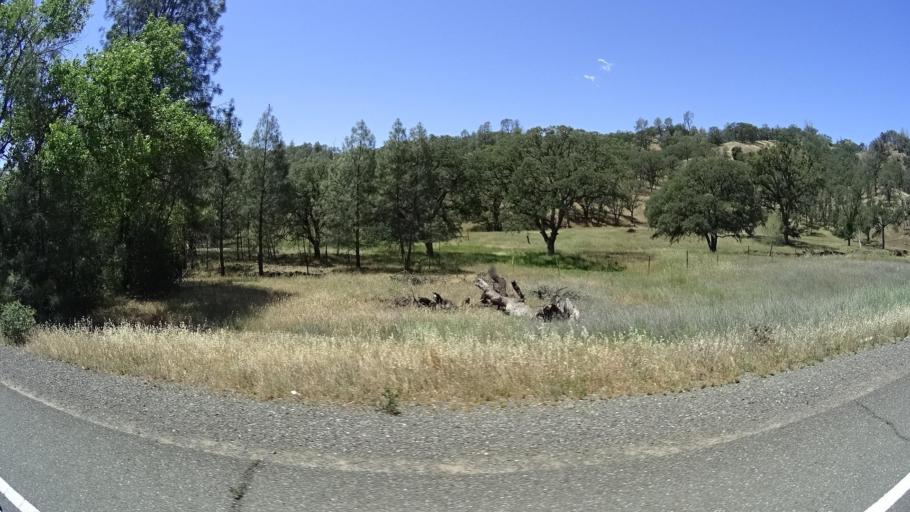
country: US
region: California
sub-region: Lake County
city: Hidden Valley Lake
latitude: 38.8223
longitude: -122.5787
